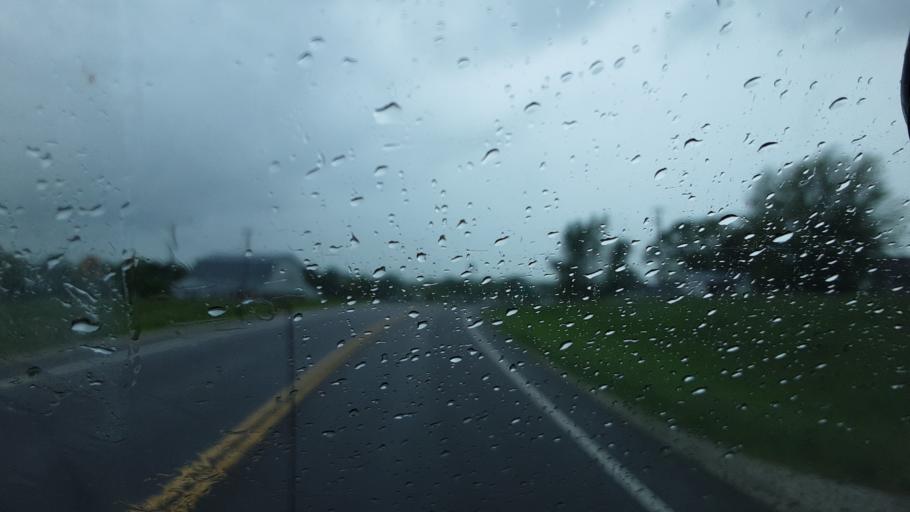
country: US
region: Missouri
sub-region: Monroe County
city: Paris
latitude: 39.4750
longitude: -92.2017
